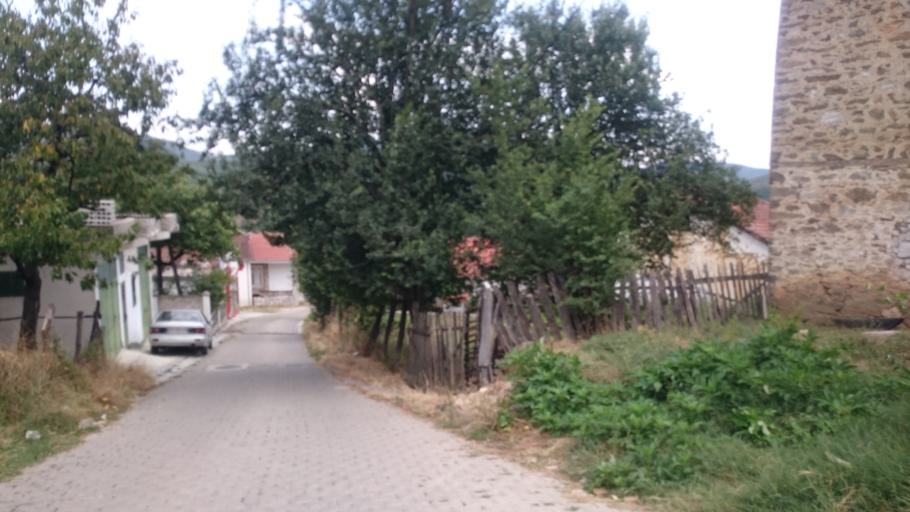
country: MK
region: Makedonski Brod
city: Makedonski Brod
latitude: 41.5160
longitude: 21.2123
